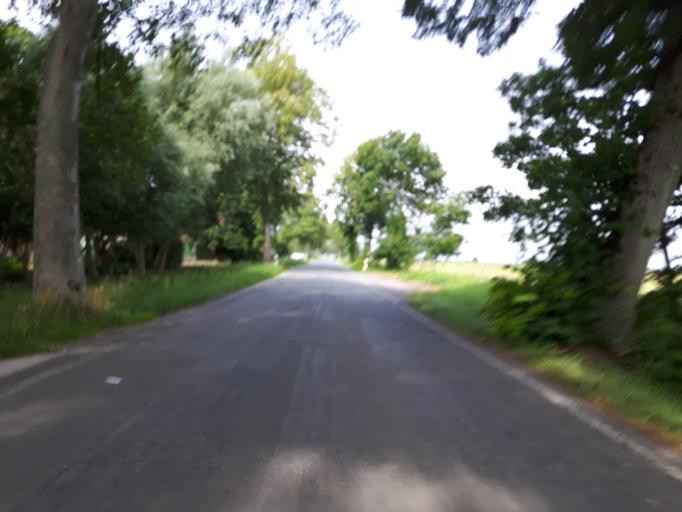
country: DE
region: Lower Saxony
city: Elsfleth
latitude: 53.2571
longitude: 8.4575
